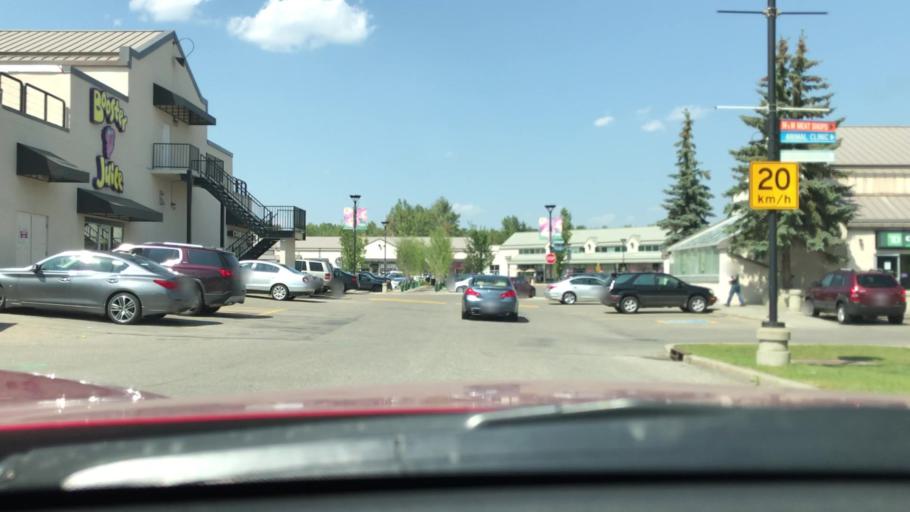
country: CA
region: Alberta
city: Calgary
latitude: 50.9728
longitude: -114.0979
